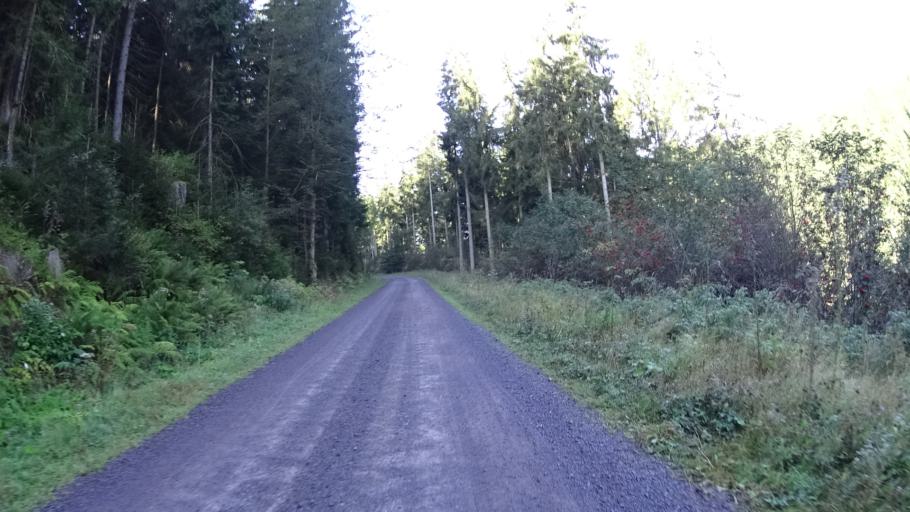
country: DE
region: Thuringia
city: Langewiesen
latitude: 50.6454
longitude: 10.9562
